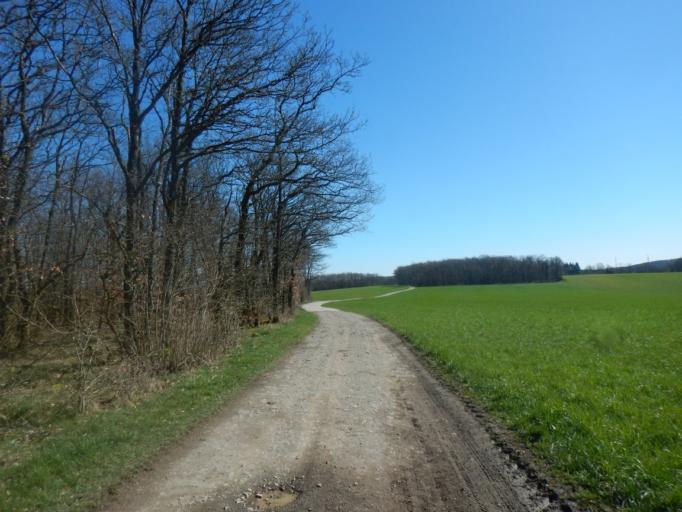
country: LU
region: Diekirch
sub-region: Canton de Wiltz
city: Eschweiler
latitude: 49.9904
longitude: 5.9320
